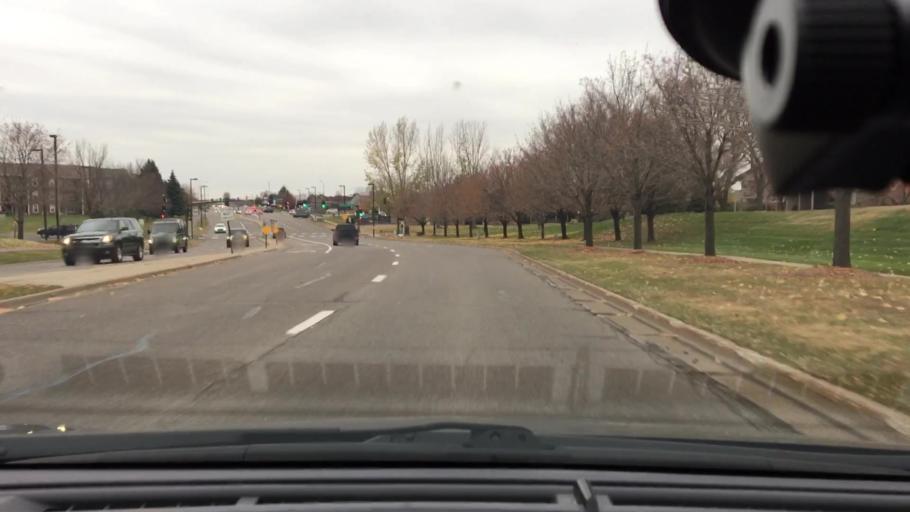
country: US
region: Minnesota
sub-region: Hennepin County
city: Maple Grove
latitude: 45.1084
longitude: -93.4518
